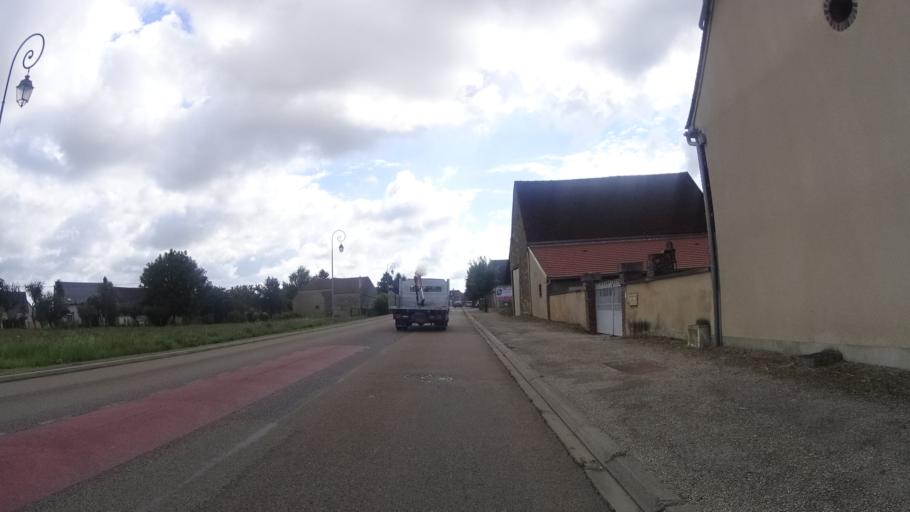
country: FR
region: Bourgogne
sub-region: Departement de l'Yonne
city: Saint-Florentin
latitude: 47.9958
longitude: 3.7748
